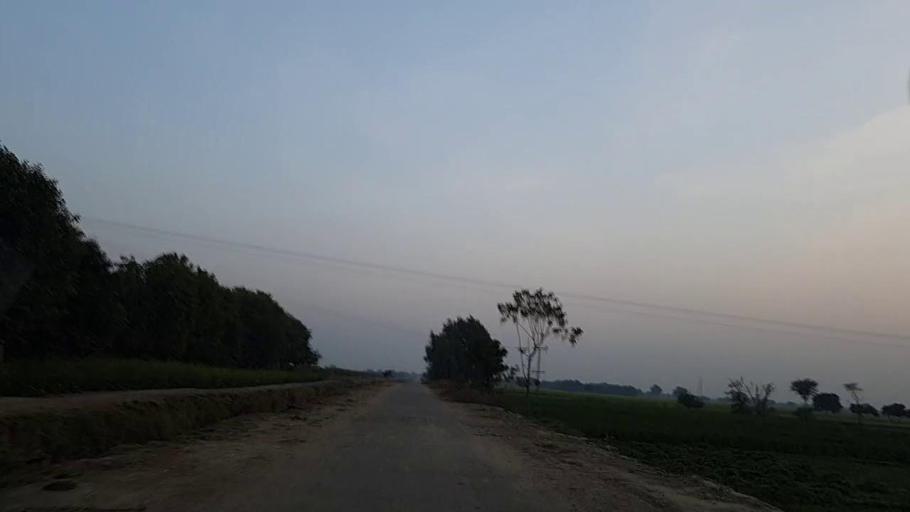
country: PK
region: Sindh
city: Tando Ghulam Ali
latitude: 25.1163
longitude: 68.8988
